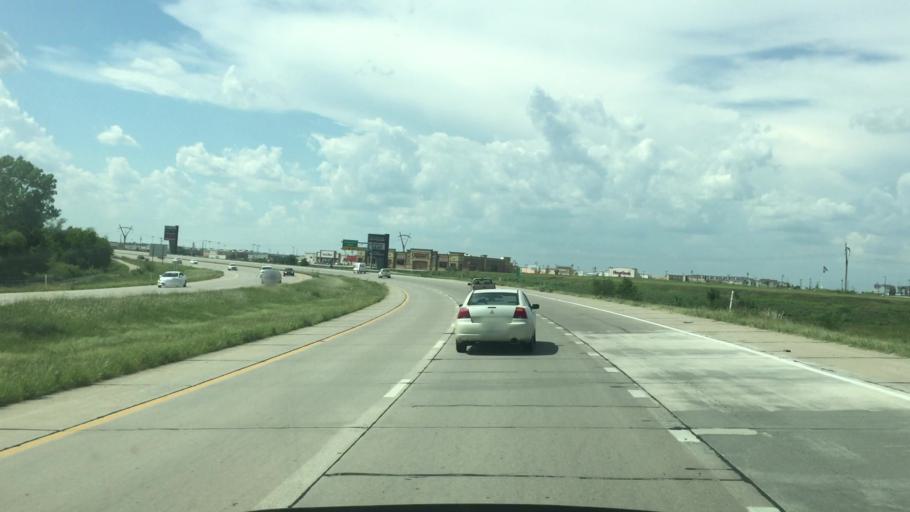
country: US
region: Kansas
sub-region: Butler County
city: Andover
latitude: 37.7271
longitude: -97.2001
